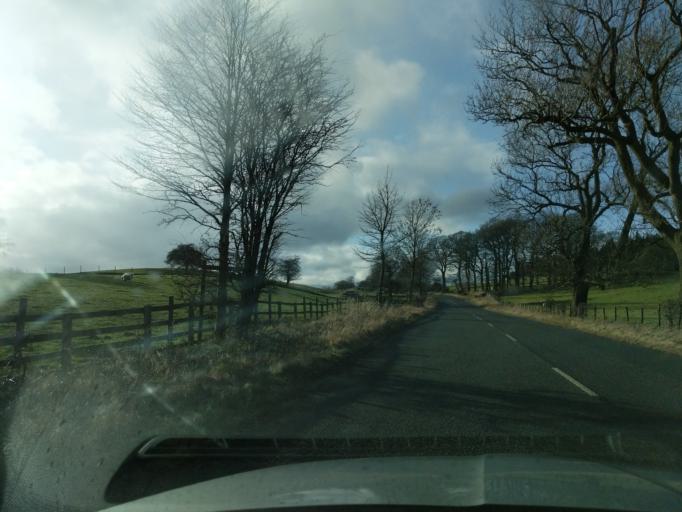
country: GB
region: England
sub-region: North Yorkshire
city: Catterick Garrison
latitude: 54.3471
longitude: -1.7499
